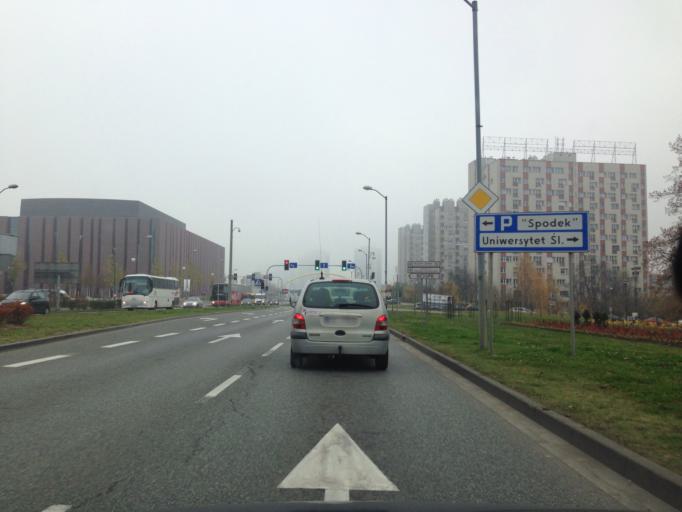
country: PL
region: Silesian Voivodeship
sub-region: Katowice
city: Katowice
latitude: 50.2639
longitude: 19.0254
